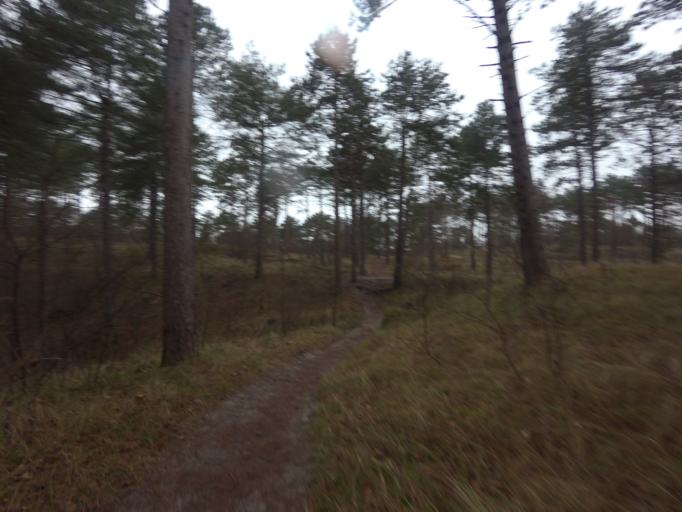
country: NL
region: Zeeland
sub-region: Schouwen-Duiveland
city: Burgh
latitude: 51.6906
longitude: 3.7023
